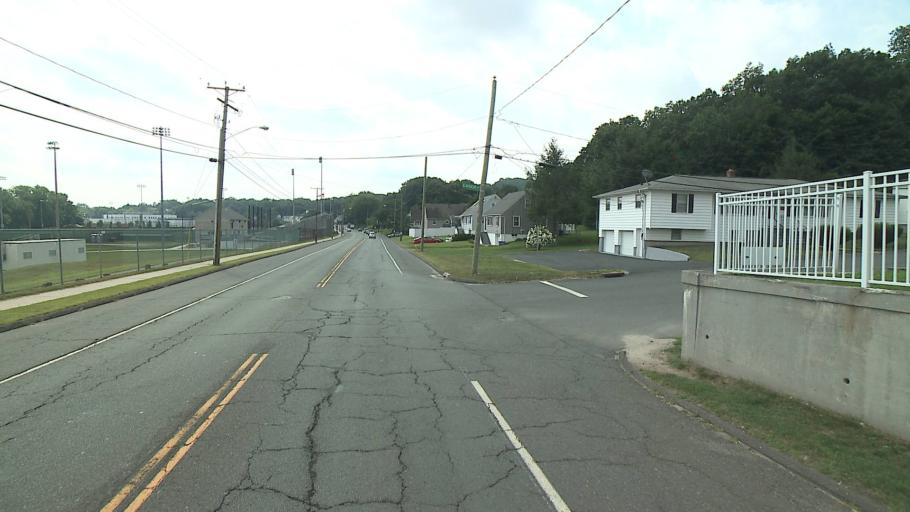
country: US
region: Connecticut
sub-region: Litchfield County
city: Oakville
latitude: 41.5789
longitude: -73.0712
